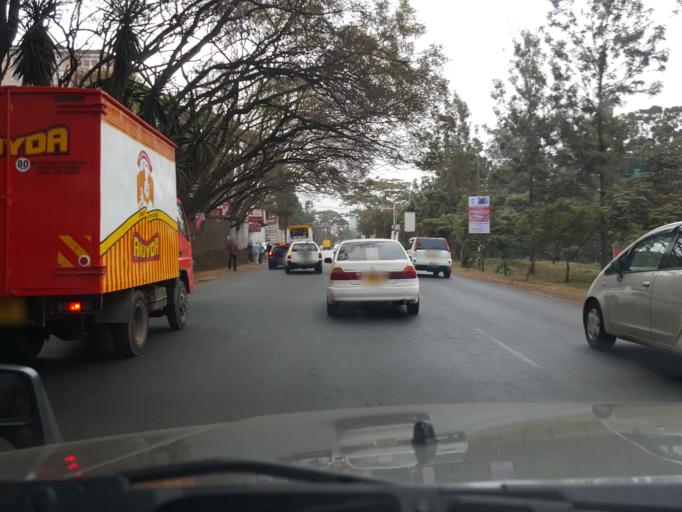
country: KE
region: Nairobi Area
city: Nairobi
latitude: -1.2704
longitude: 36.8073
